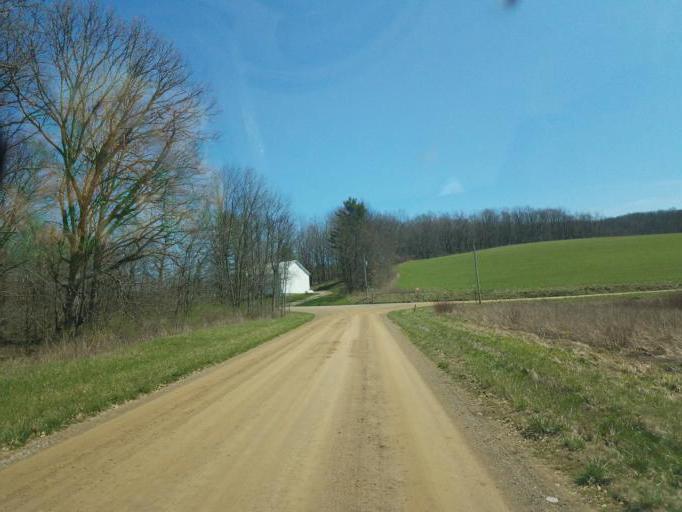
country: US
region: Ohio
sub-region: Knox County
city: Oak Hill
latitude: 40.3051
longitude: -82.2354
